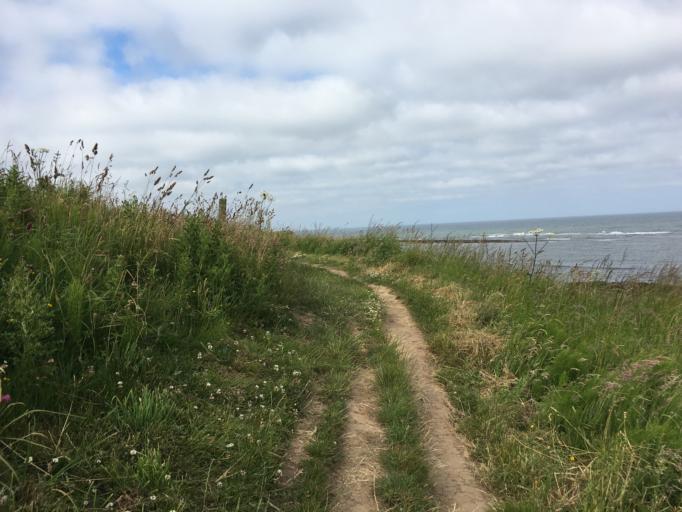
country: GB
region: England
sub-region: Northumberland
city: Alnmouth
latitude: 55.4437
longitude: -1.5901
